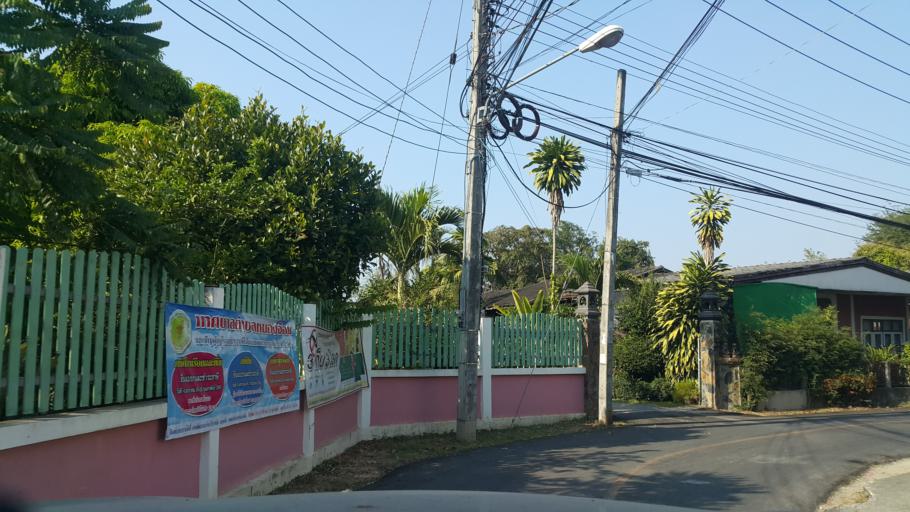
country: TH
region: Chiang Mai
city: San Sai
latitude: 18.8568
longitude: 99.0240
